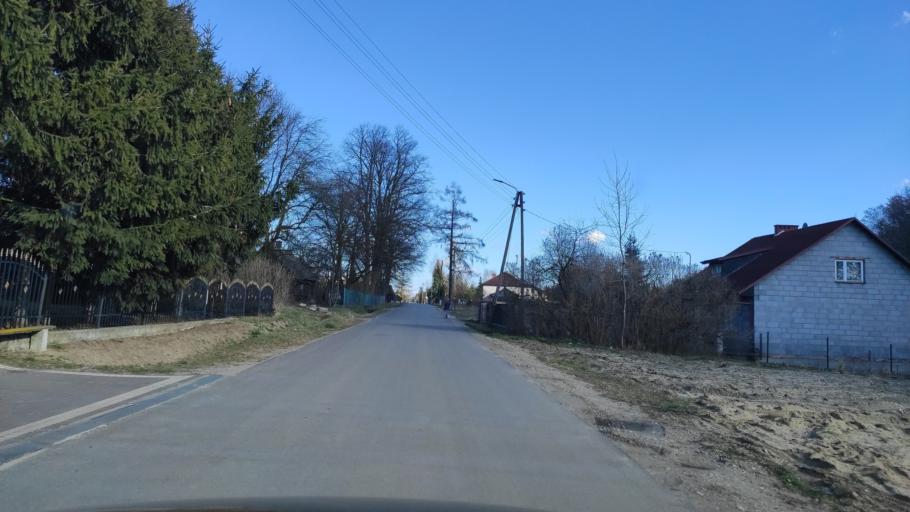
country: PL
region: Masovian Voivodeship
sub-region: Powiat radomski
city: Jedlnia-Letnisko
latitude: 51.4399
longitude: 21.2969
